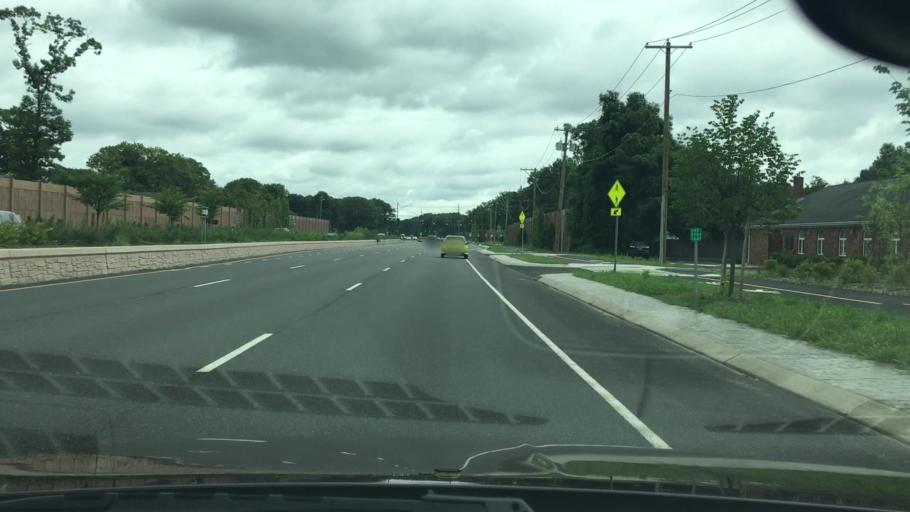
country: US
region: New York
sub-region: Suffolk County
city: Nesconset
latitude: 40.8519
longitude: -73.1569
